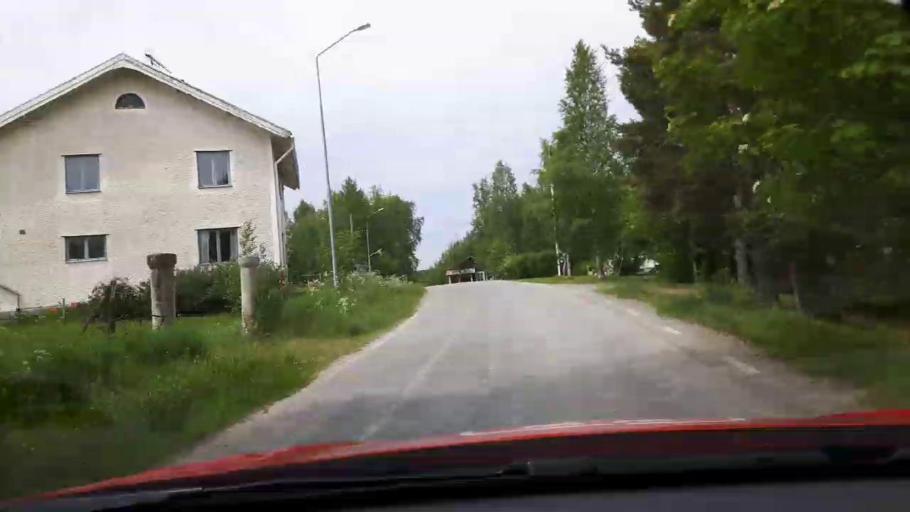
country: SE
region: Jaemtland
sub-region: Harjedalens Kommun
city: Sveg
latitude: 62.4079
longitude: 13.6917
